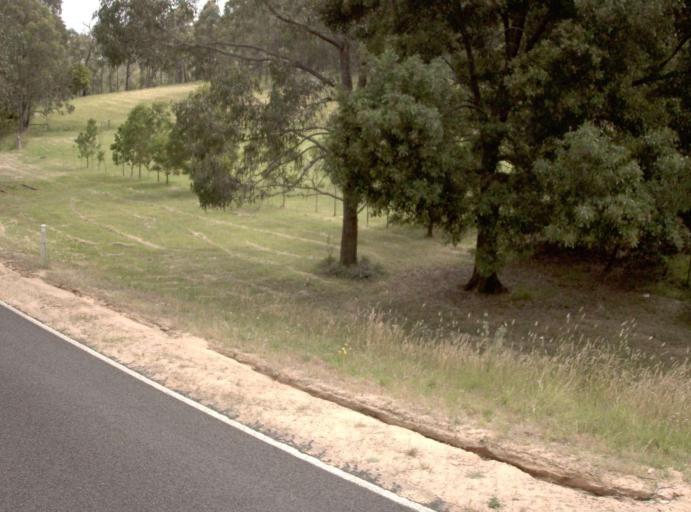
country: AU
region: Victoria
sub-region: Latrobe
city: Traralgon
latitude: -38.4062
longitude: 146.8242
